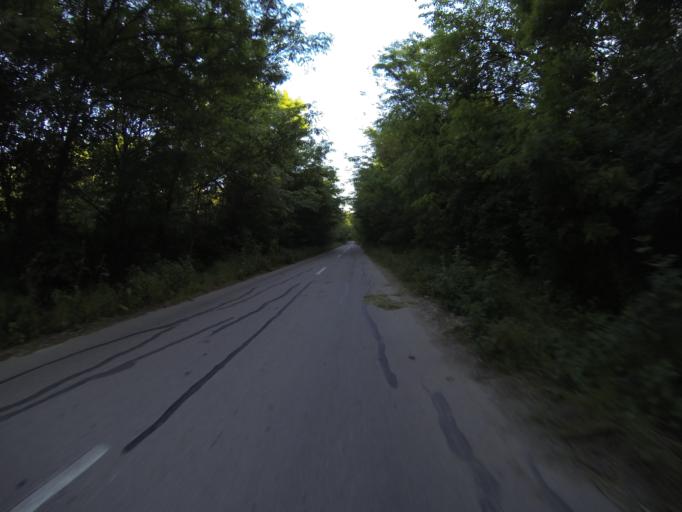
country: RO
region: Dolj
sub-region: Comuna Tuglui
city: Tuglui
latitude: 44.1763
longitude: 23.8163
